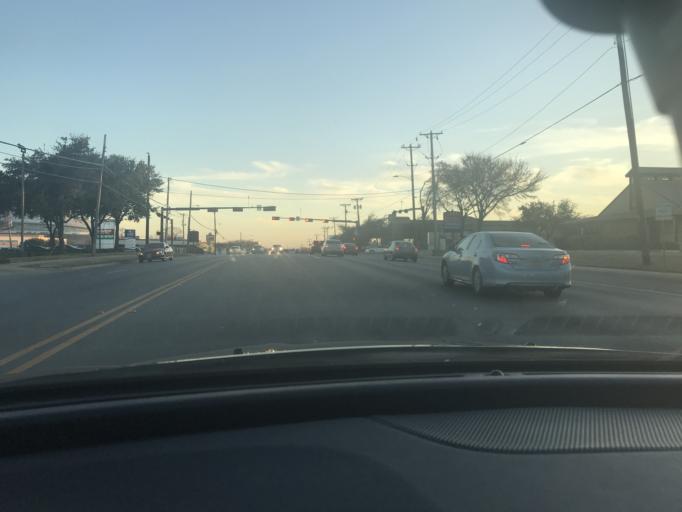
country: US
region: Texas
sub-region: Tarrant County
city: Arlington
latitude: 32.7564
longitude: -97.0973
